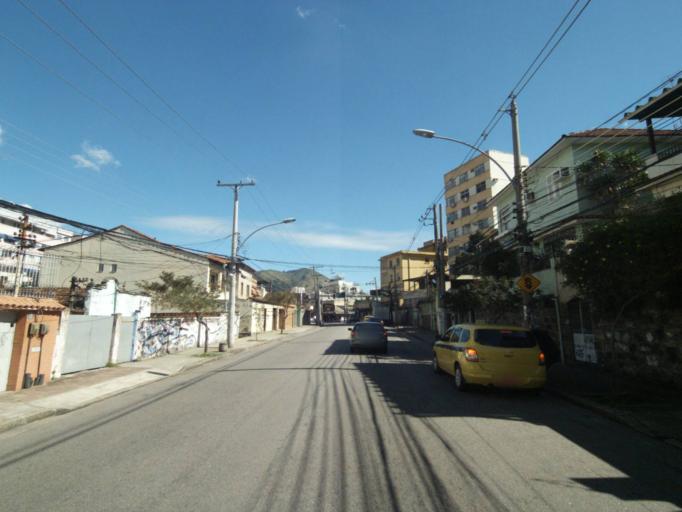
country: BR
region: Rio de Janeiro
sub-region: Rio De Janeiro
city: Rio de Janeiro
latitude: -22.9095
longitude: -43.2818
